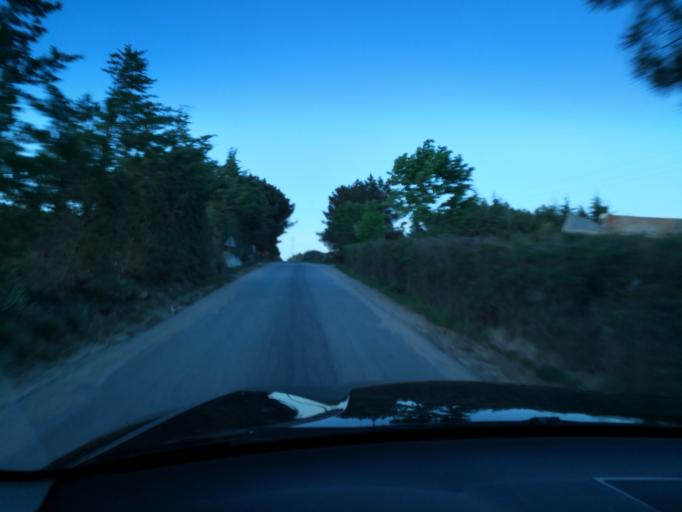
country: PT
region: Vila Real
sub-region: Vila Real
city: Vila Real
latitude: 41.3458
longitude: -7.6920
